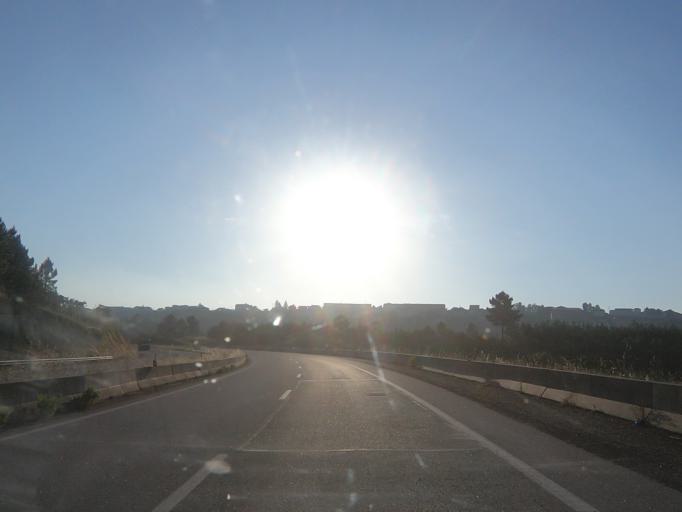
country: PT
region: Guarda
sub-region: Celorico da Beira
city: Celorico da Beira
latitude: 40.6277
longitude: -7.3832
